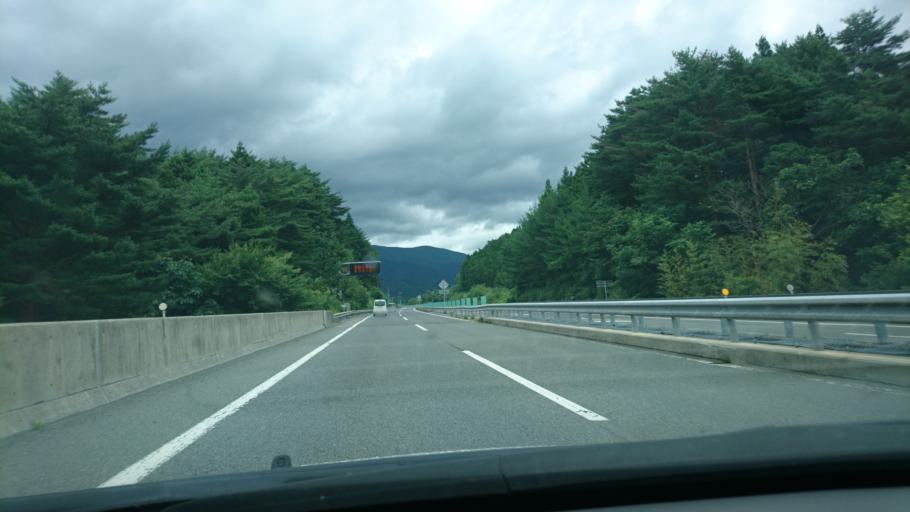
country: JP
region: Iwate
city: Ofunato
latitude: 39.1024
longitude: 141.7048
